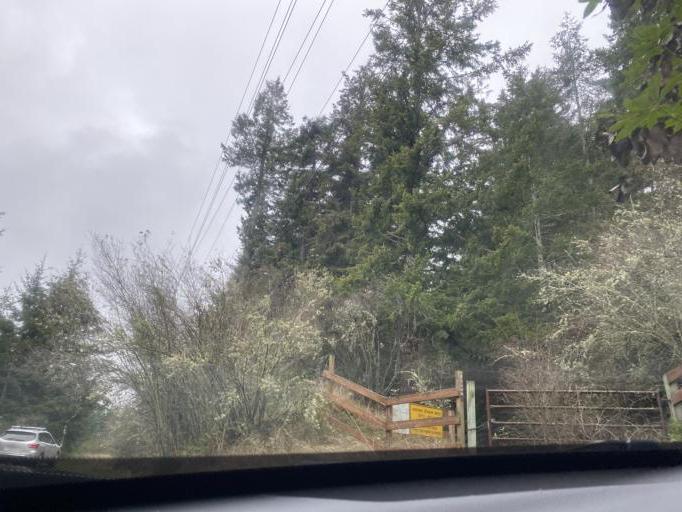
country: US
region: Washington
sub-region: Island County
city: Camano
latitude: 48.1142
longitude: -122.5839
